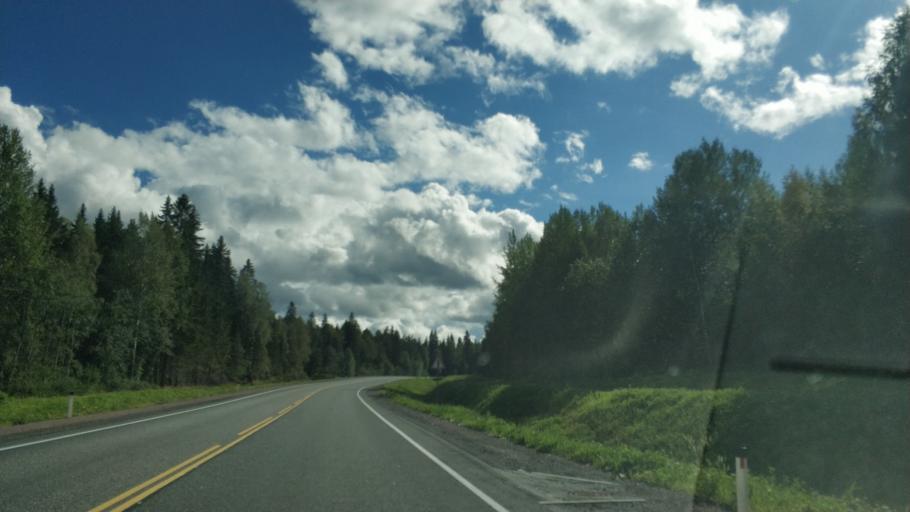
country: RU
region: Republic of Karelia
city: Ruskeala
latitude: 61.8701
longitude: 30.6517
